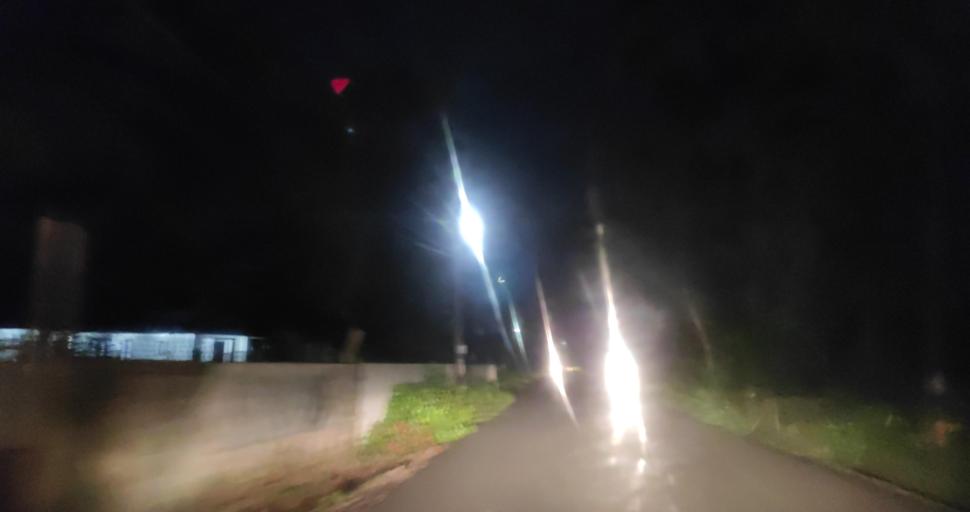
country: IN
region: Kerala
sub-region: Alappuzha
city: Vayalar
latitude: 9.6820
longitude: 76.3030
